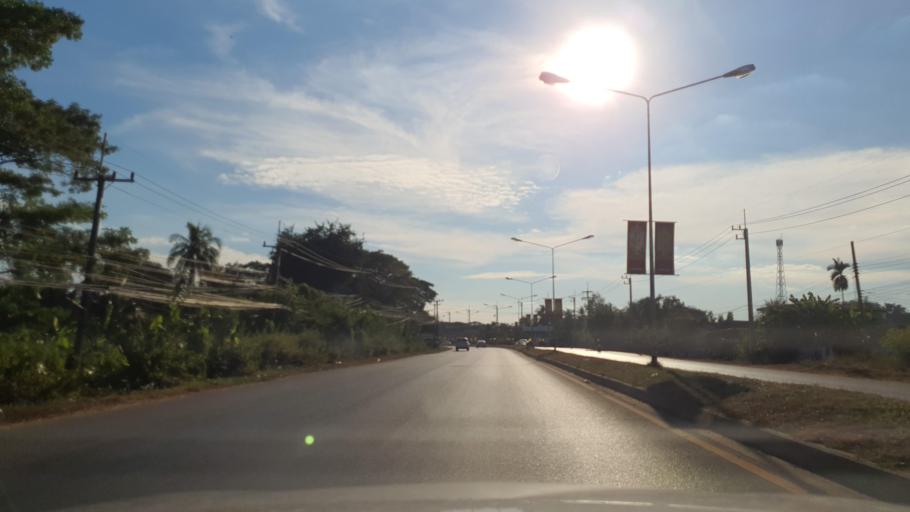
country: TH
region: Maha Sarakham
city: Kantharawichai
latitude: 16.3287
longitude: 103.3008
